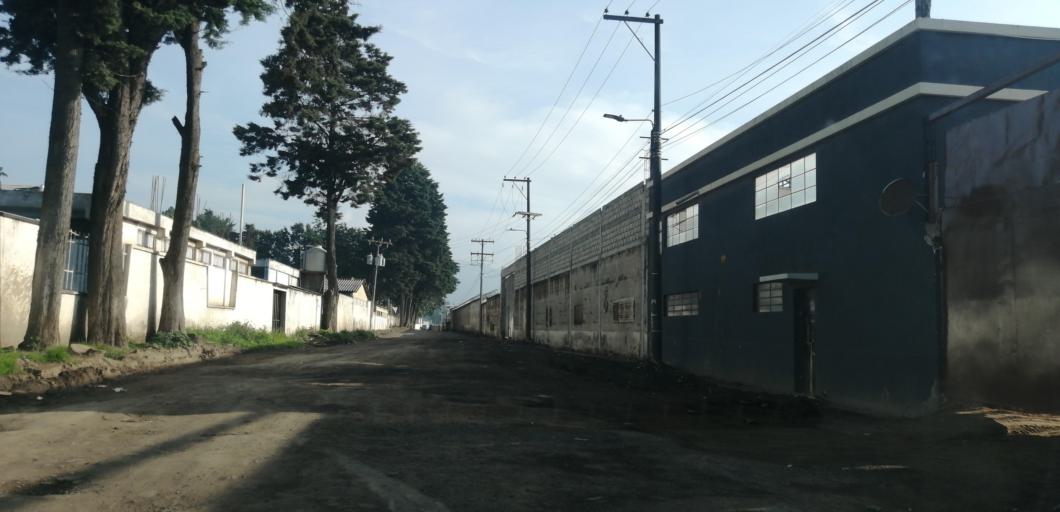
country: GT
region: Quetzaltenango
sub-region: Municipio de La Esperanza
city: La Esperanza
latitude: 14.8572
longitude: -91.5389
